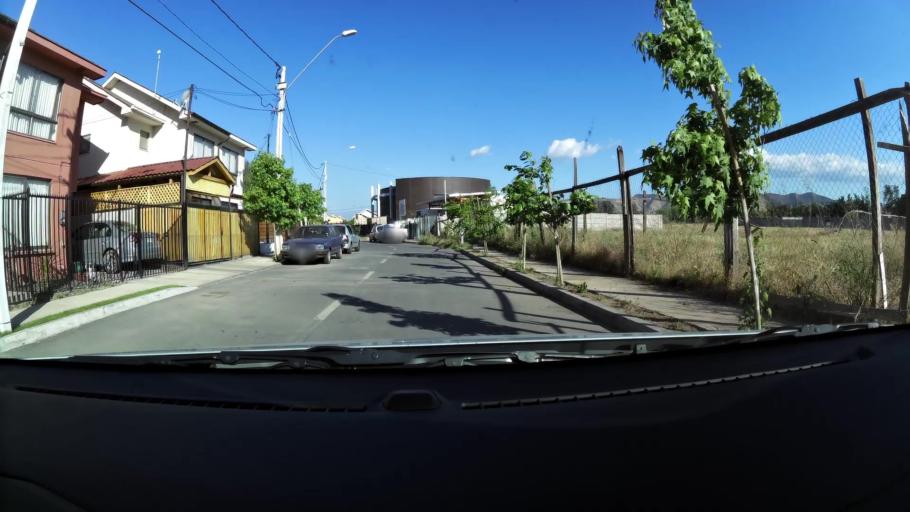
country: CL
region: Santiago Metropolitan
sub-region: Provincia de Maipo
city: San Bernardo
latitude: -33.5520
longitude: -70.7652
